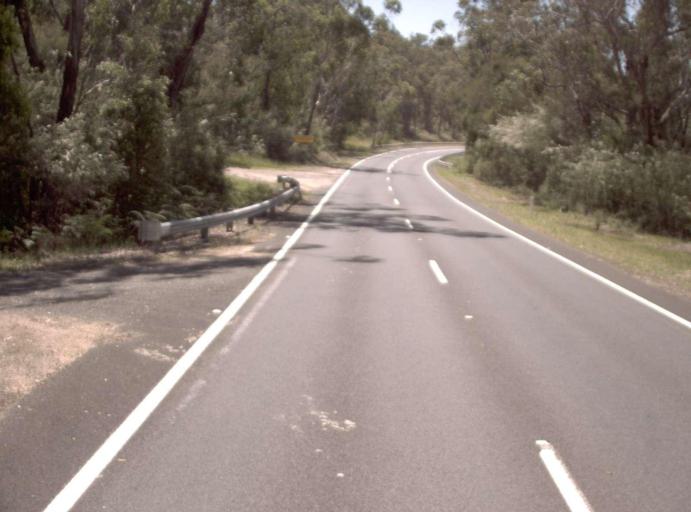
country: AU
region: Victoria
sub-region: East Gippsland
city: Lakes Entrance
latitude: -37.7365
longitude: 148.0818
